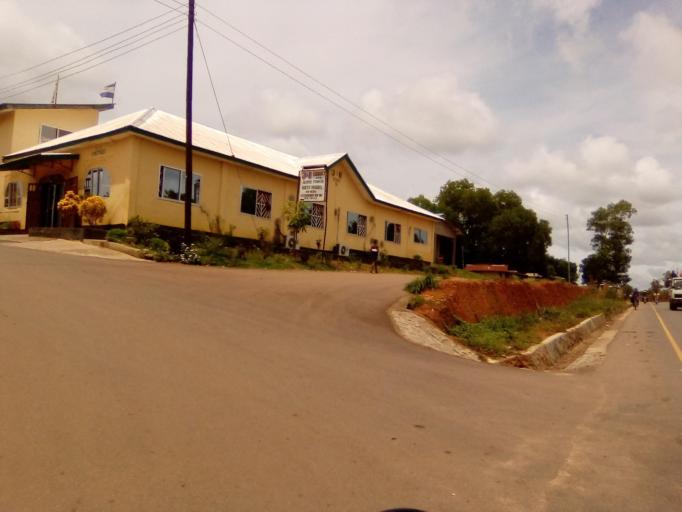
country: SL
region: Southern Province
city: Bo
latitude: 7.9326
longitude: -11.7249
